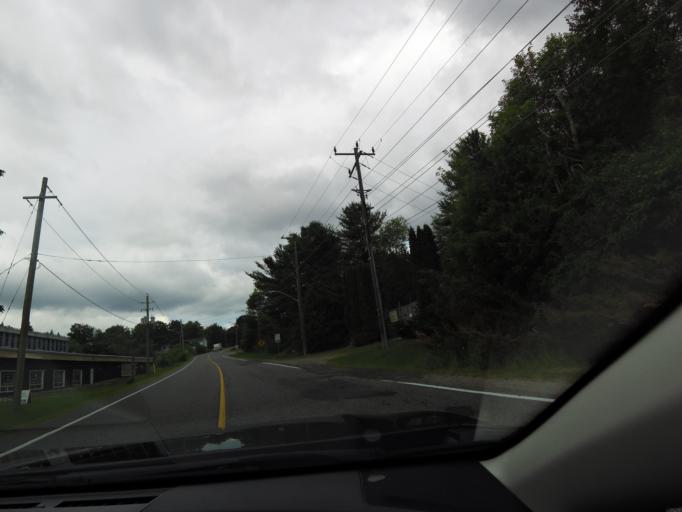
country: CA
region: Ontario
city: Bracebridge
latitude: 45.0359
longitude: -79.3046
